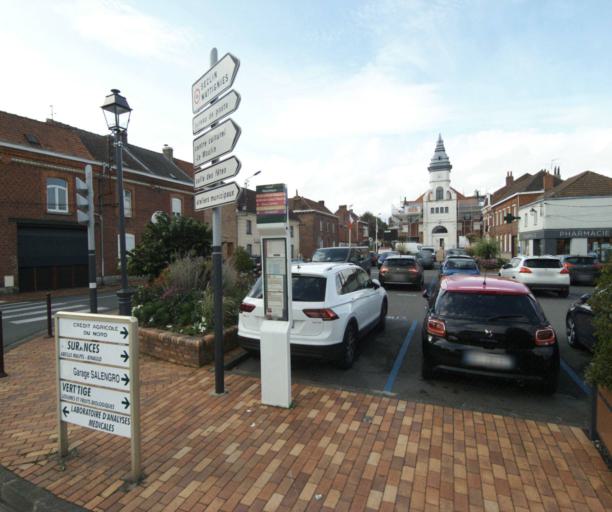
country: FR
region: Nord-Pas-de-Calais
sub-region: Departement du Nord
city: Wavrin
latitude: 50.5689
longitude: 2.9316
